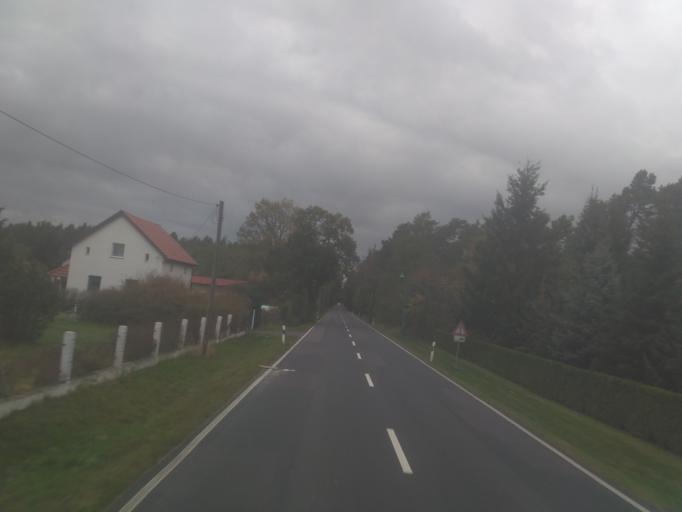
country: DE
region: Brandenburg
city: Merzdorf
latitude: 51.3873
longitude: 13.5108
